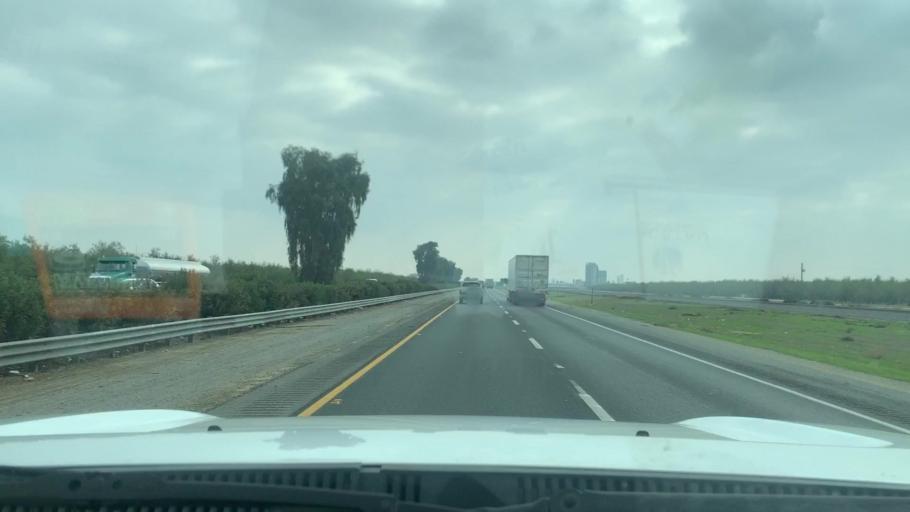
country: US
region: California
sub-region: Tulare County
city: Tipton
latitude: 36.0209
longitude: -119.3055
